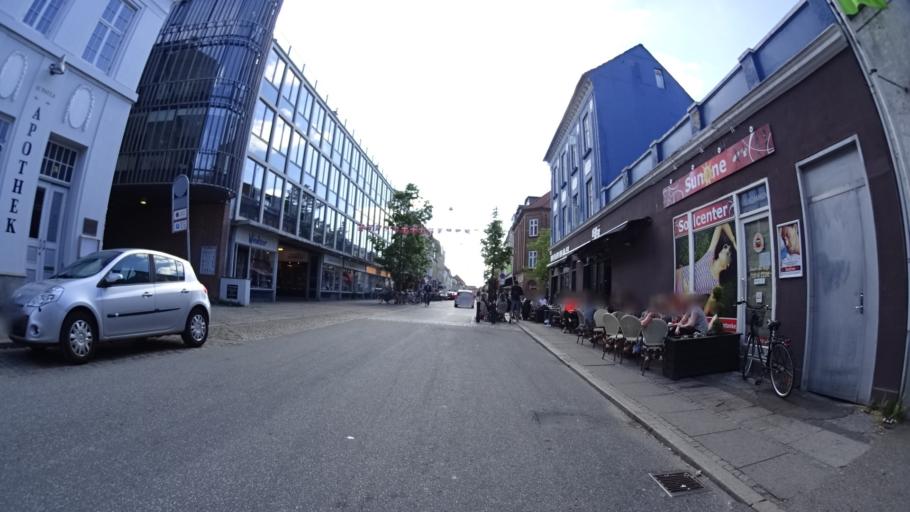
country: DK
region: Central Jutland
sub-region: Arhus Kommune
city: Arhus
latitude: 56.1479
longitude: 10.2017
